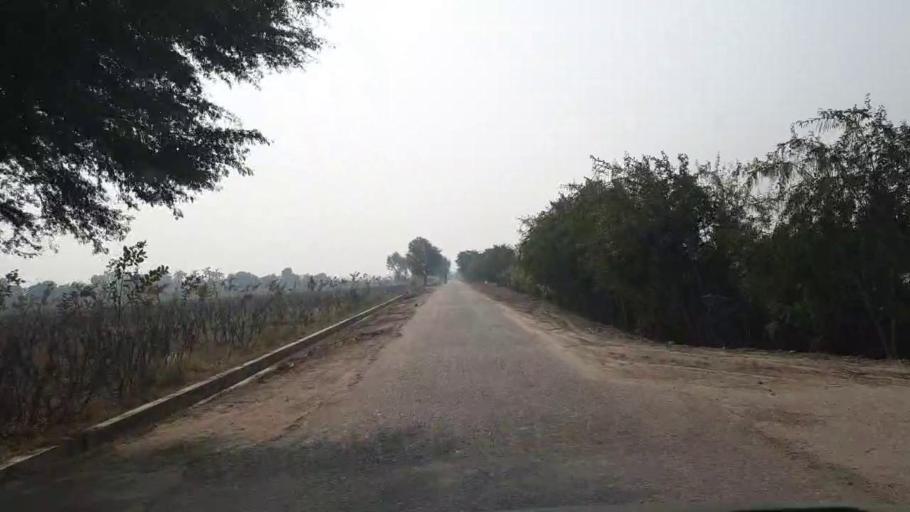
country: PK
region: Sindh
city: Hala
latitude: 25.8254
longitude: 68.4377
